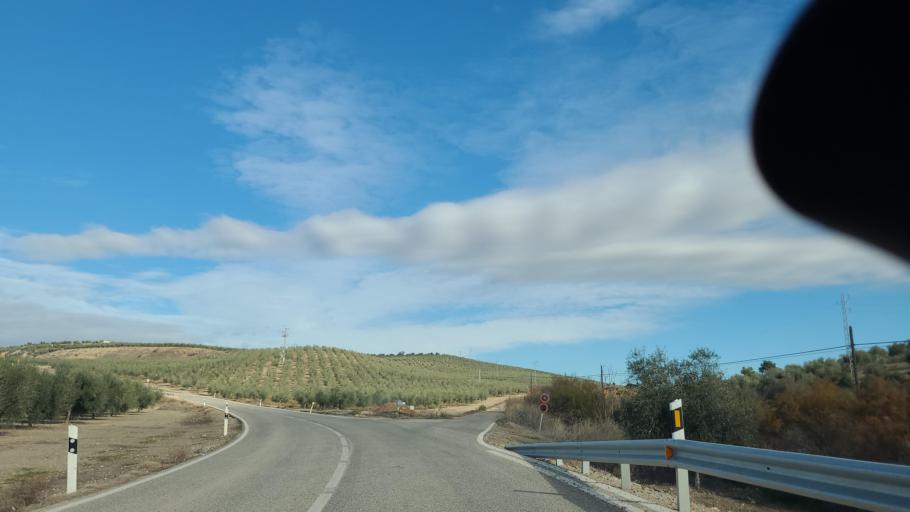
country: ES
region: Andalusia
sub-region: Provincia de Jaen
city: Espeluy
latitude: 38.0148
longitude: -3.8852
